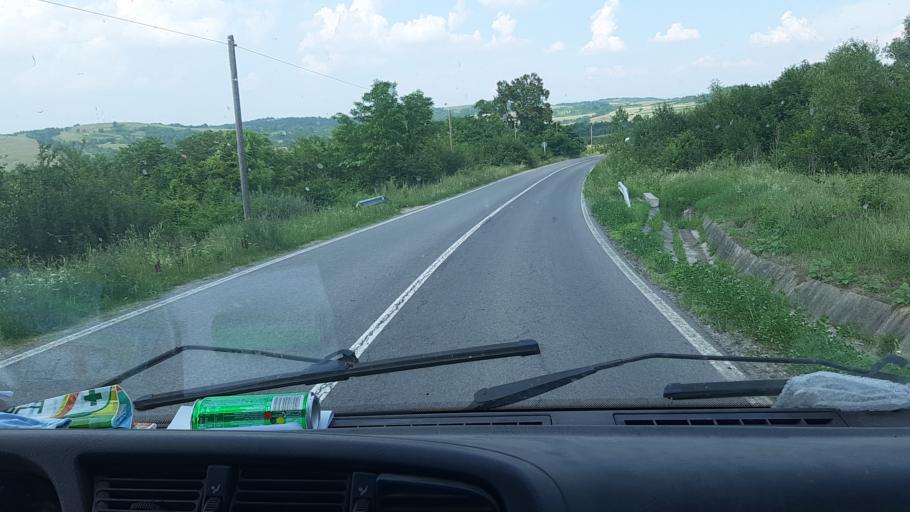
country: RO
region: Caras-Severin
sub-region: Comuna Farliug
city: Farliug
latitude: 45.5009
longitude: 21.8579
